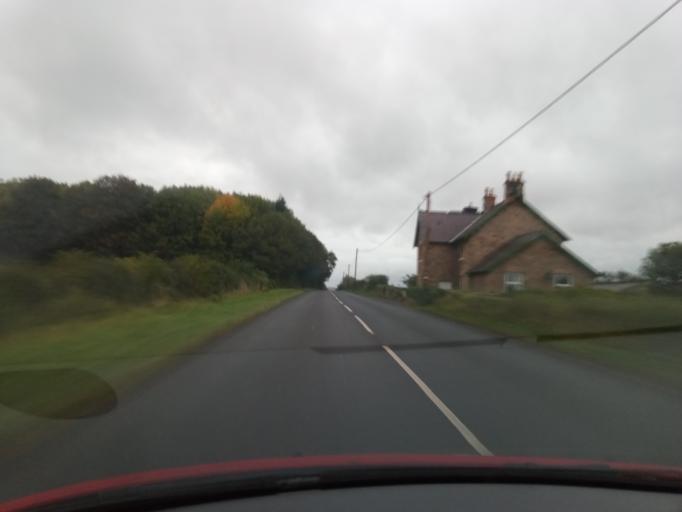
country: GB
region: England
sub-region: Darlington
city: High Coniscliffe
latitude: 54.5234
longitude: -1.6720
